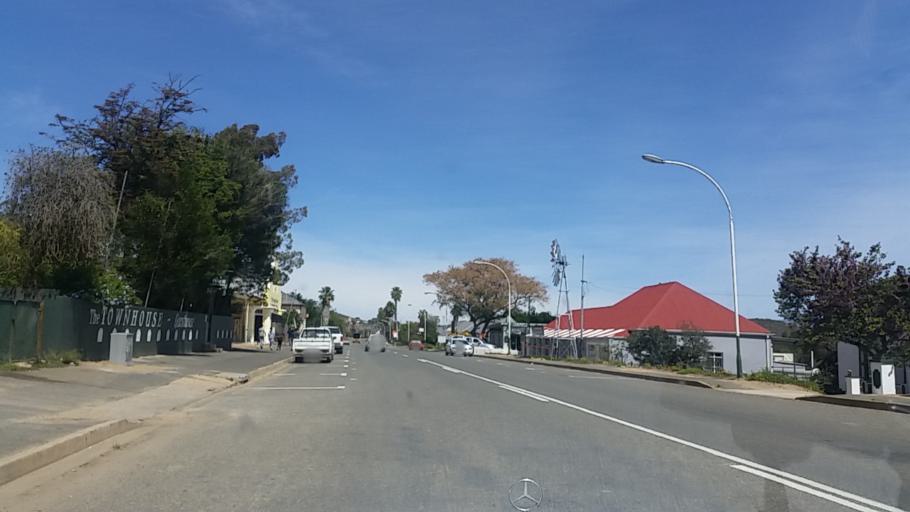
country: ZA
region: Western Cape
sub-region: Eden District Municipality
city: Knysna
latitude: -33.6548
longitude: 23.1300
